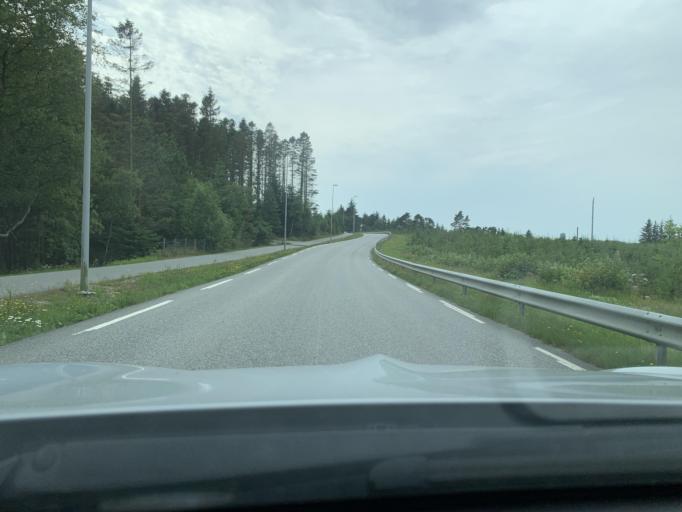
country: NO
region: Rogaland
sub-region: Time
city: Bryne
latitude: 58.7512
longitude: 5.6957
